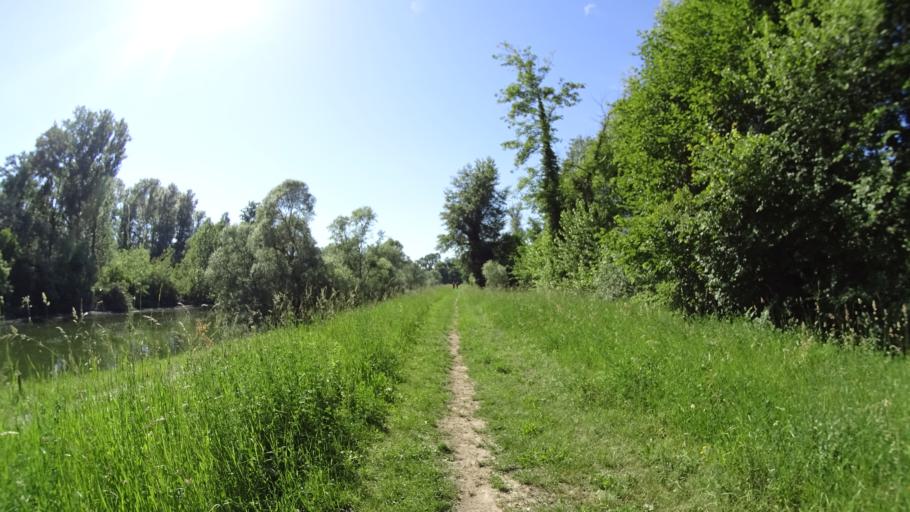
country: DE
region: Baden-Wuerttemberg
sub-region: Karlsruhe Region
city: Eggenstein-Leopoldshafen
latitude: 49.1030
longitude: 8.3693
